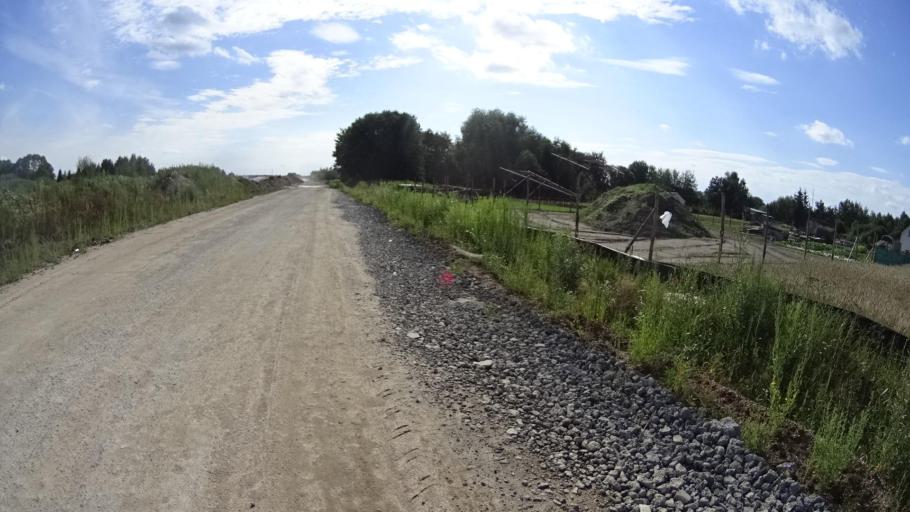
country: PL
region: Masovian Voivodeship
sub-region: Powiat piaseczynski
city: Lesznowola
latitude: 52.0599
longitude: 20.9318
